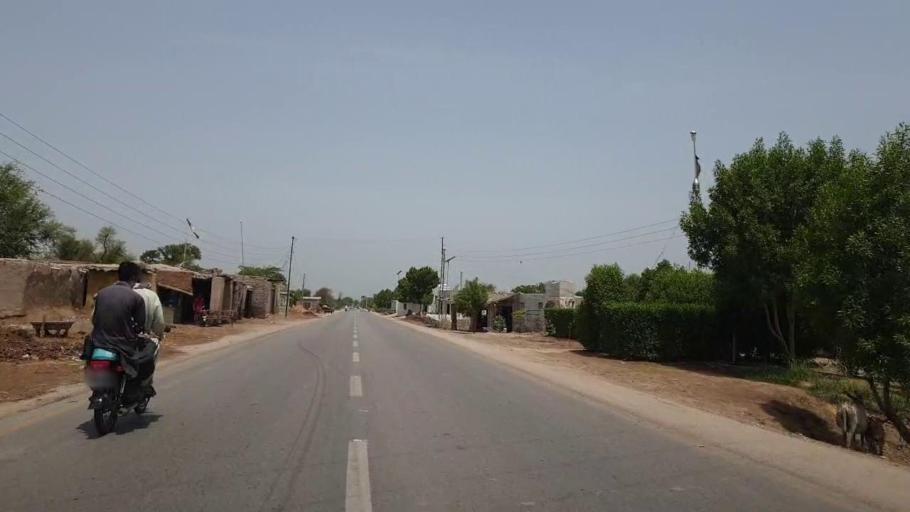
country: PK
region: Sindh
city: Nawabshah
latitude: 26.2372
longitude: 68.4756
